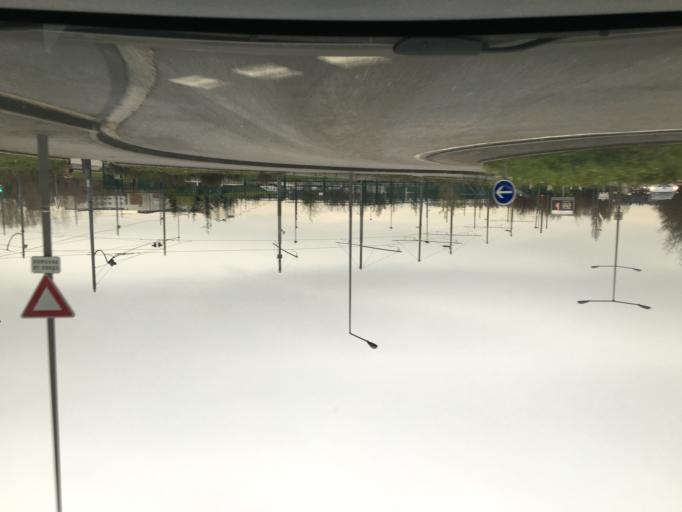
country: FR
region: Rhone-Alpes
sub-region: Departement du Rhone
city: Bron
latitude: 45.7200
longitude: 4.9240
